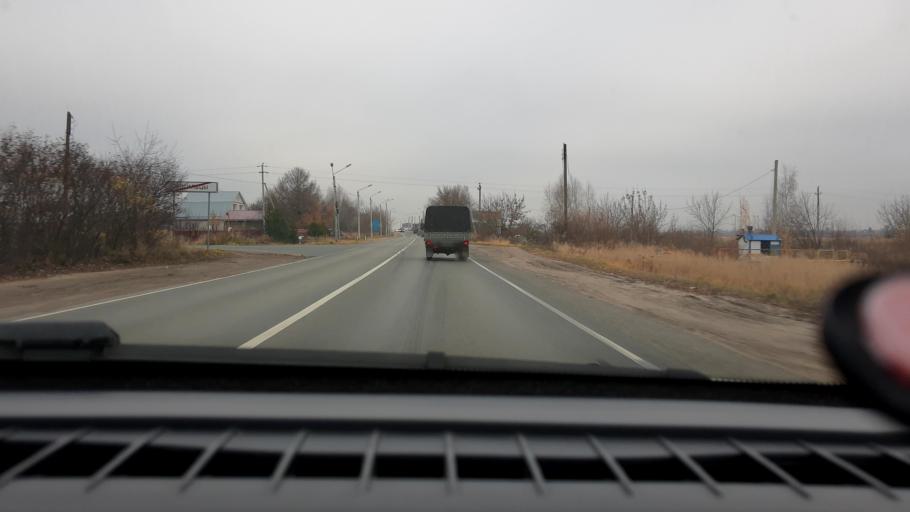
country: RU
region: Nizjnij Novgorod
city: Gidrotorf
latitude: 56.5489
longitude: 43.5233
